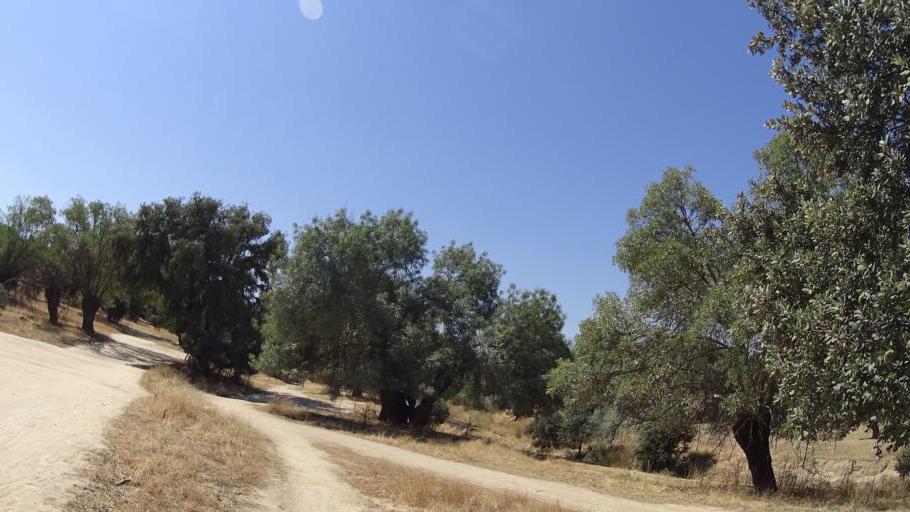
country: ES
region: Madrid
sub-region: Provincia de Madrid
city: Boadilla del Monte
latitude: 40.4150
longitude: -3.8603
